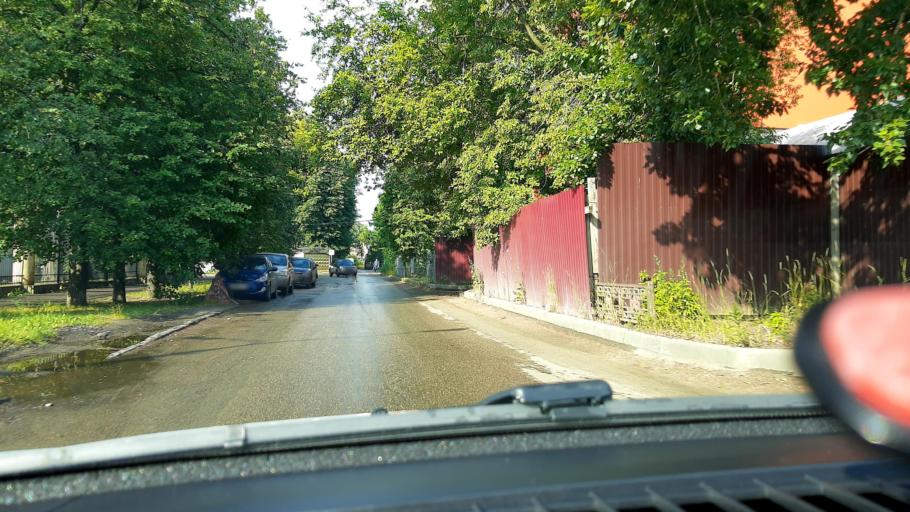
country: RU
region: Nizjnij Novgorod
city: Nizhniy Novgorod
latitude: 56.2547
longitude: 43.8893
